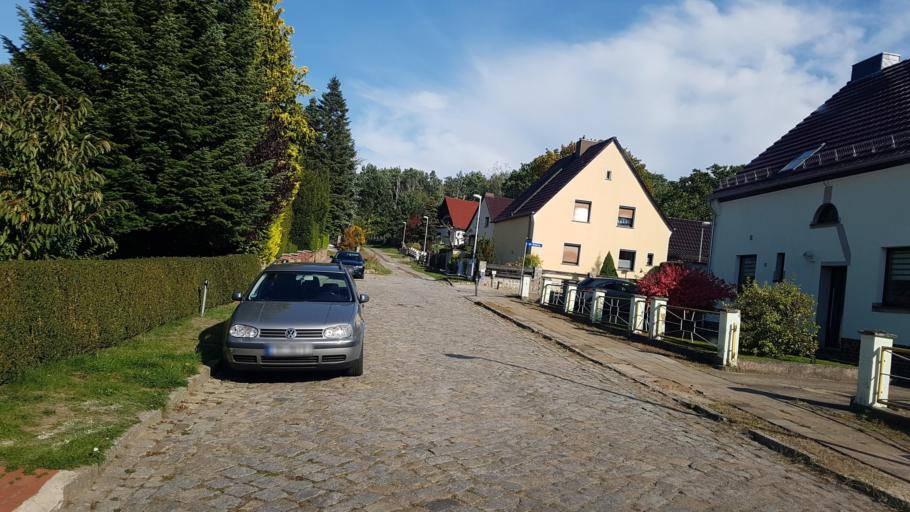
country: DE
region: Brandenburg
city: Belzig
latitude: 52.1451
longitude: 12.6029
